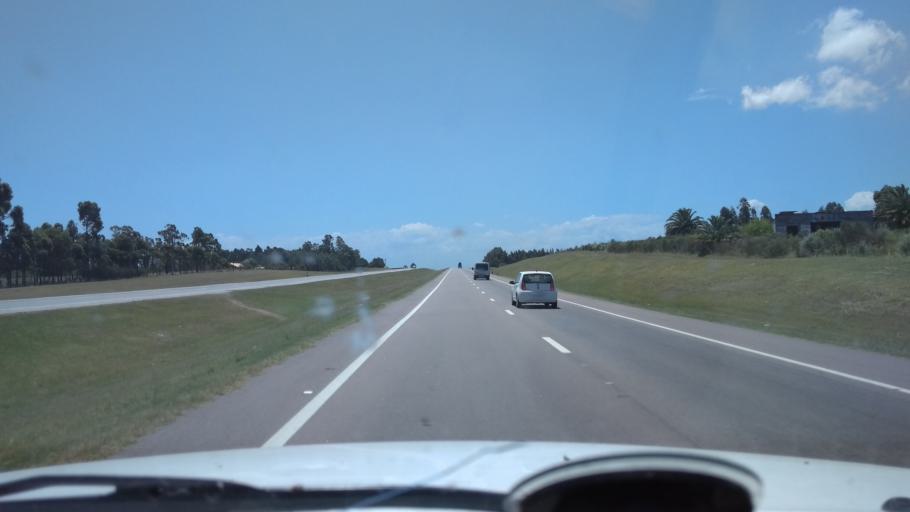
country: UY
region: Canelones
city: Progreso
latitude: -34.6628
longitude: -56.2406
